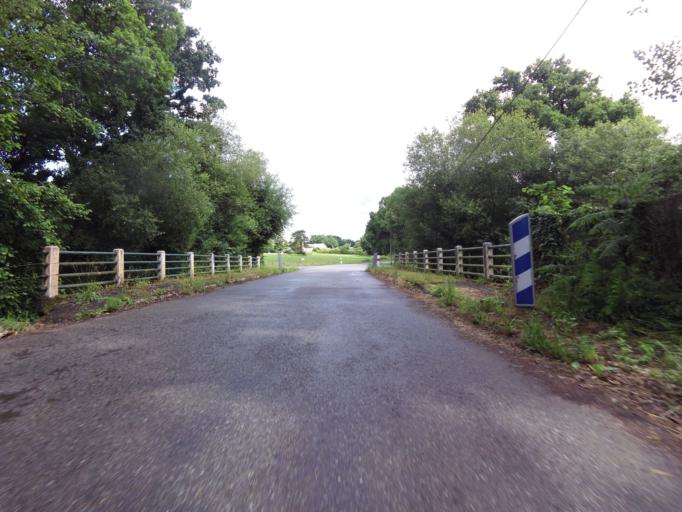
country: FR
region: Brittany
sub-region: Departement du Morbihan
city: Malansac
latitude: 47.7052
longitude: -2.2804
